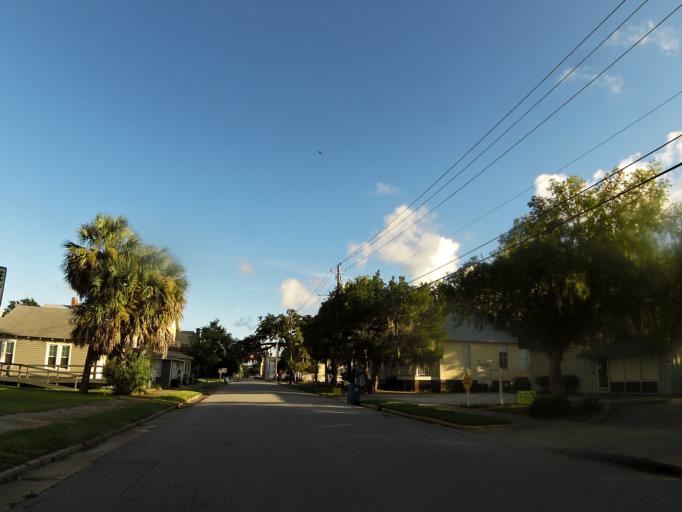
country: US
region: Georgia
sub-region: Glynn County
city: Brunswick
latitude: 31.1517
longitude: -81.4949
